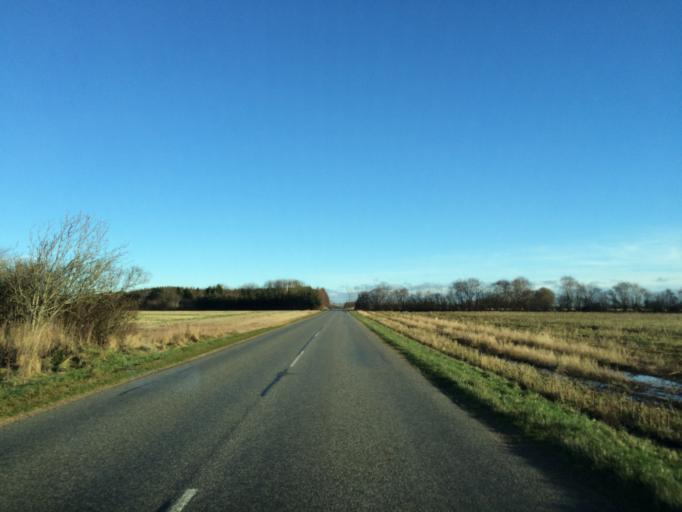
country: DK
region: Central Jutland
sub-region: Ringkobing-Skjern Kommune
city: Videbaek
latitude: 56.0846
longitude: 8.6799
